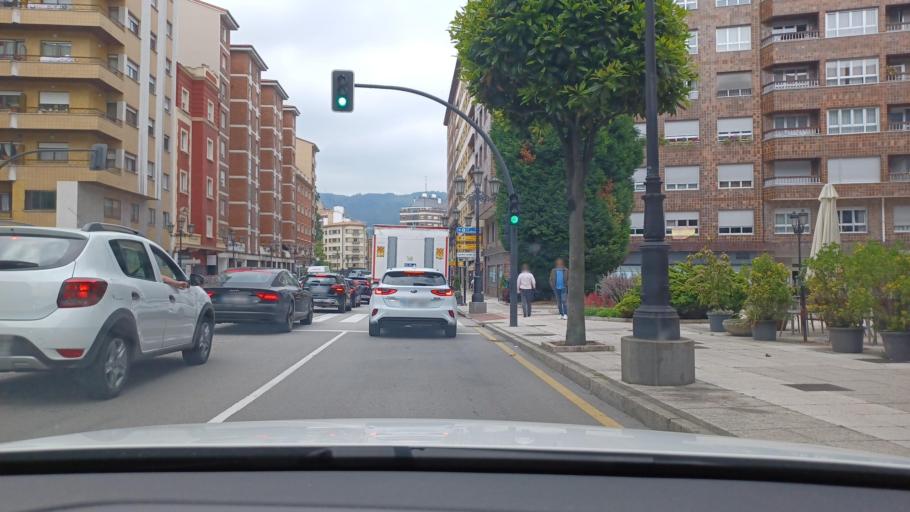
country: ES
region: Asturias
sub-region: Province of Asturias
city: Oviedo
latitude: 43.3596
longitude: -5.8584
